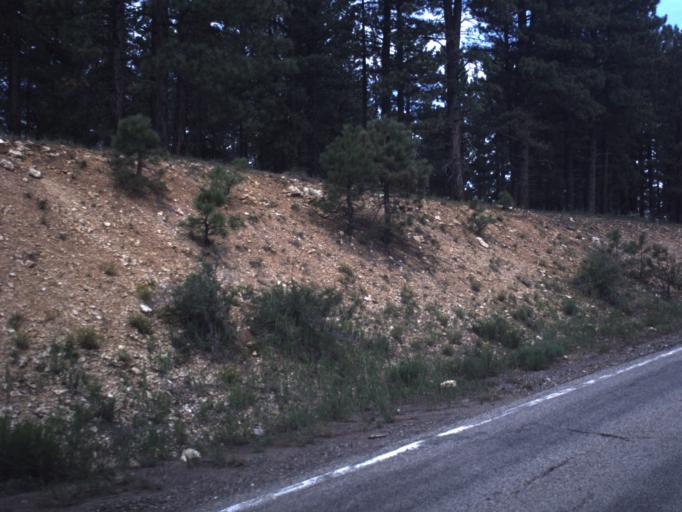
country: US
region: Utah
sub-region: Garfield County
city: Panguitch
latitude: 37.4963
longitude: -112.6208
